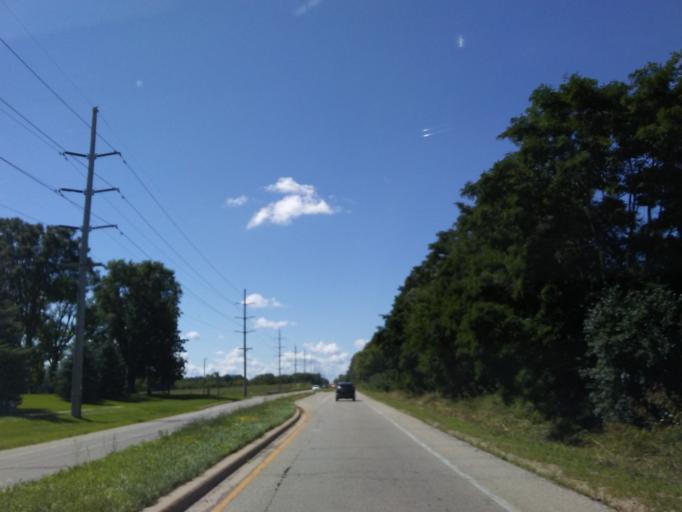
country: US
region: Wisconsin
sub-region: Dane County
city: Verona
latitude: 43.0262
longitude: -89.5334
